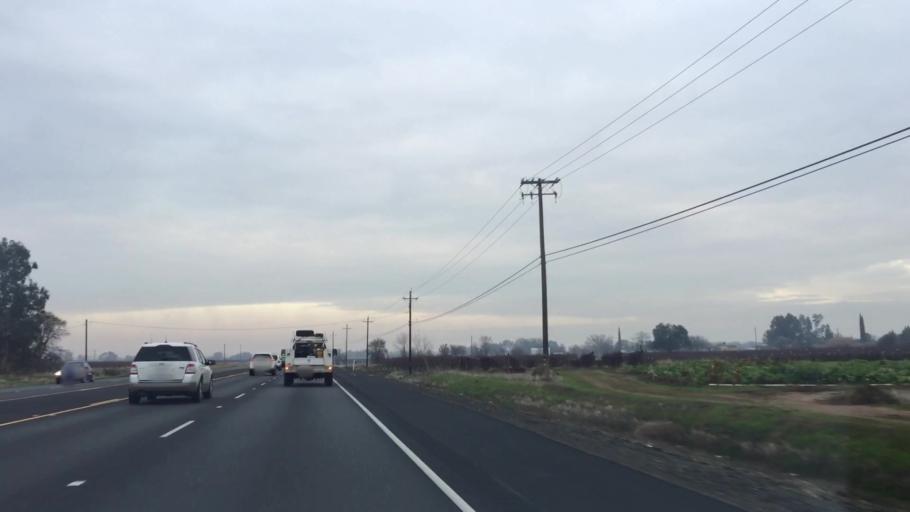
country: US
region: California
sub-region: Butte County
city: Gridley
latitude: 39.3669
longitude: -121.6088
